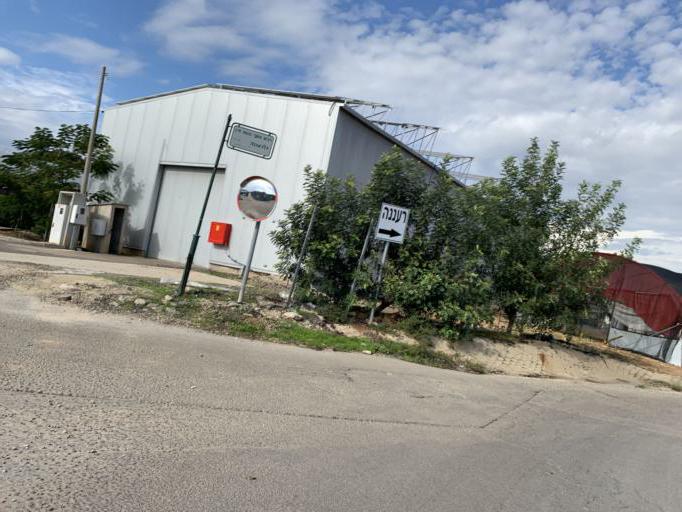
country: IL
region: Central District
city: Ra'anana
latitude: 32.1694
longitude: 34.8780
